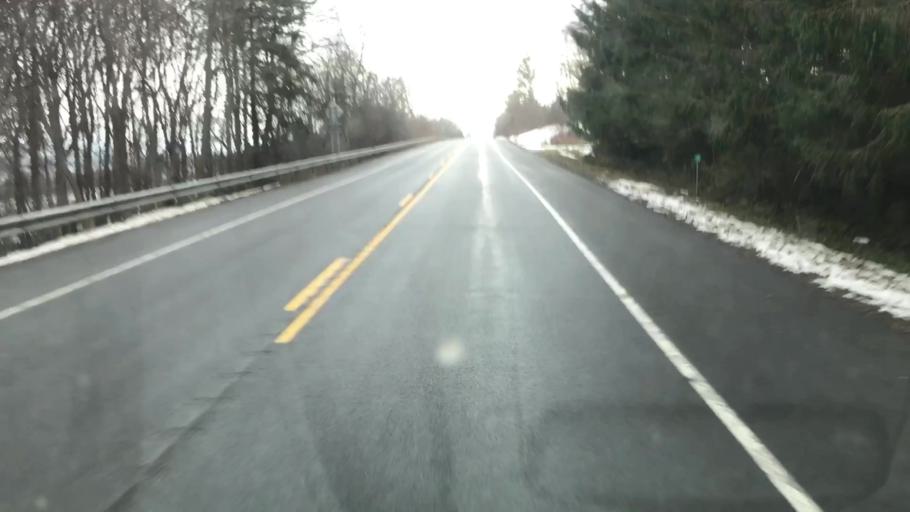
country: US
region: New York
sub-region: Onondaga County
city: Skaneateles
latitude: 42.9079
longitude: -76.4260
